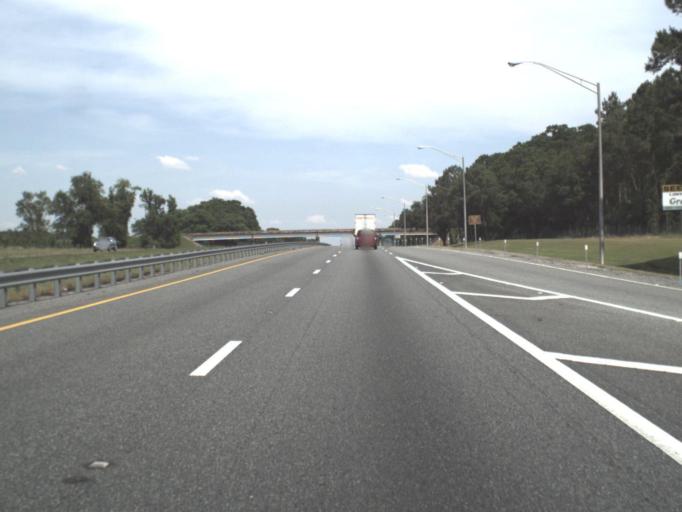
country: US
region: Florida
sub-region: Suwannee County
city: Wellborn
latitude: 30.2745
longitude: -82.7981
